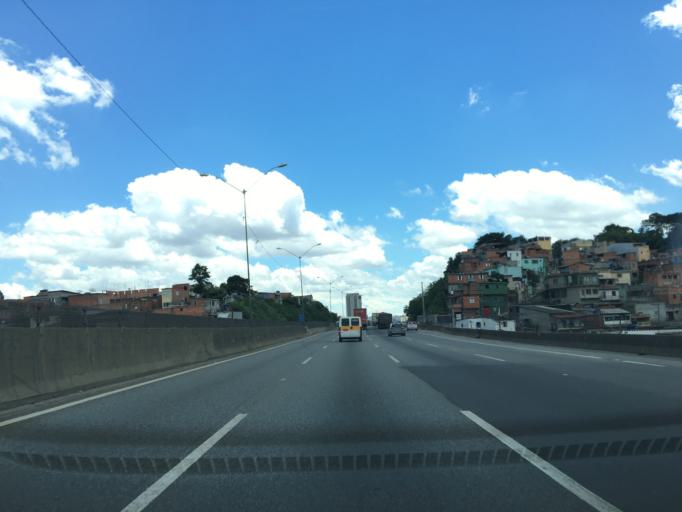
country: BR
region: Sao Paulo
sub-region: Guarulhos
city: Guarulhos
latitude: -23.4375
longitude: -46.5681
